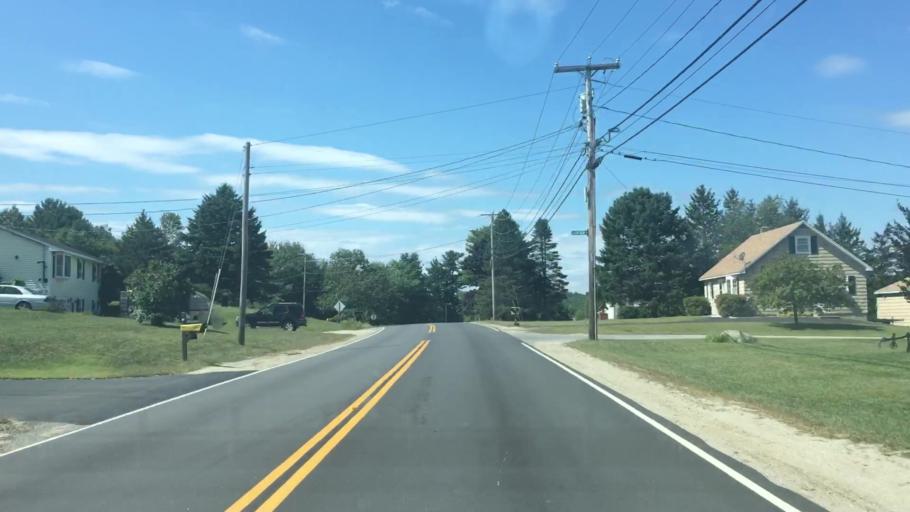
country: US
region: Maine
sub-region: Androscoggin County
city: Sabattus
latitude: 44.0763
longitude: -70.1160
